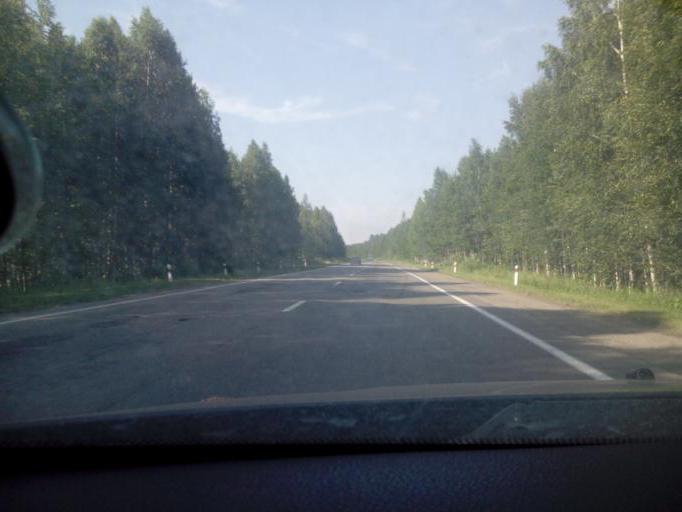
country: RU
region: Sverdlovsk
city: Verkh-Neyvinskiy
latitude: 57.2667
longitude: 60.2929
